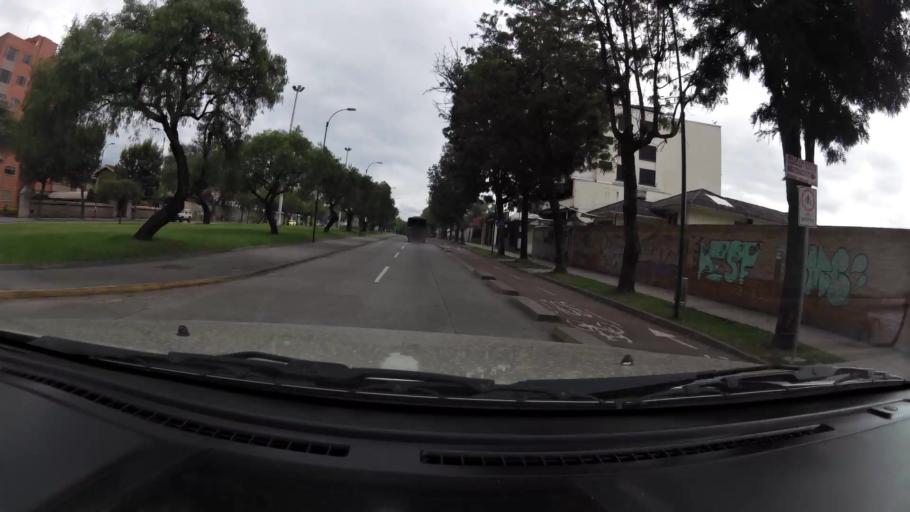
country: EC
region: Azuay
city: Cuenca
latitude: -2.9134
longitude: -79.0091
